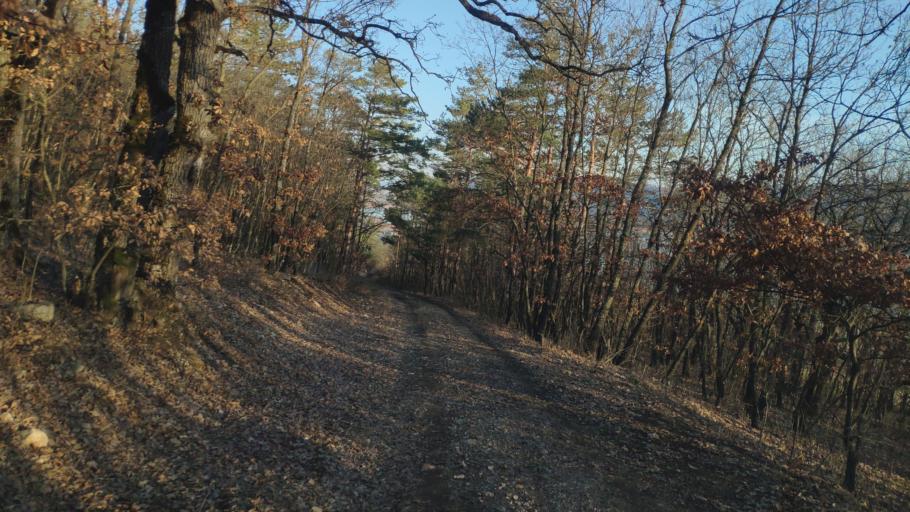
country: SK
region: Kosicky
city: Medzev
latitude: 48.6036
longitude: 20.7304
